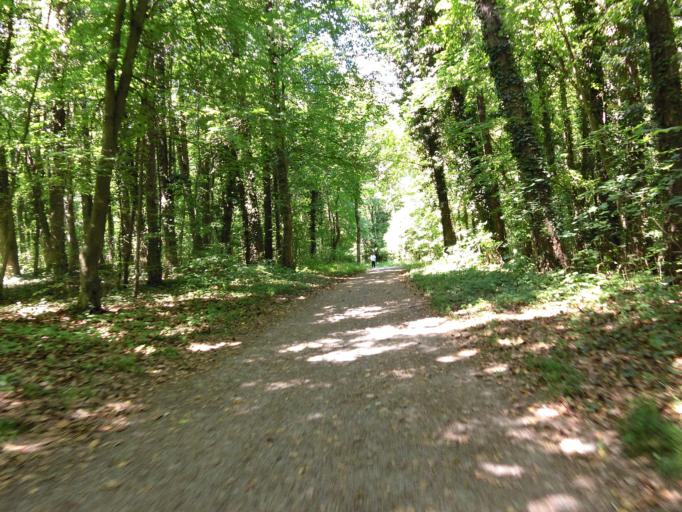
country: DE
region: Bavaria
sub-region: Regierungsbezirk Unterfranken
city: Hochberg
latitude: 49.7827
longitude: 9.9167
